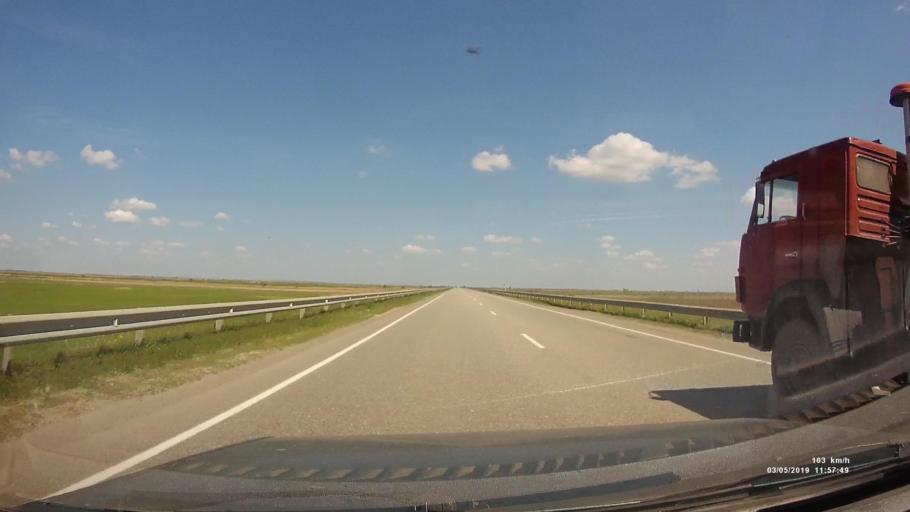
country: RU
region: Rostov
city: Bagayevskaya
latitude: 47.2117
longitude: 40.3134
